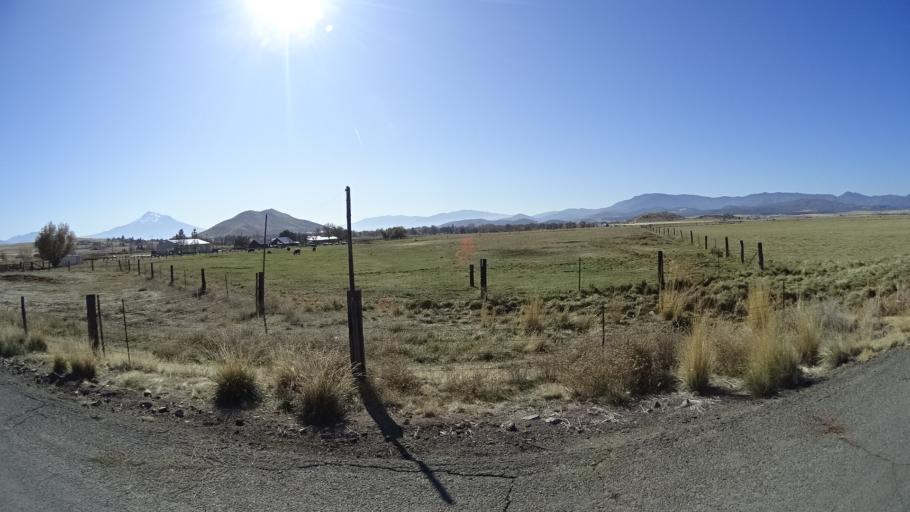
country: US
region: California
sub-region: Siskiyou County
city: Montague
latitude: 41.7420
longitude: -122.5290
